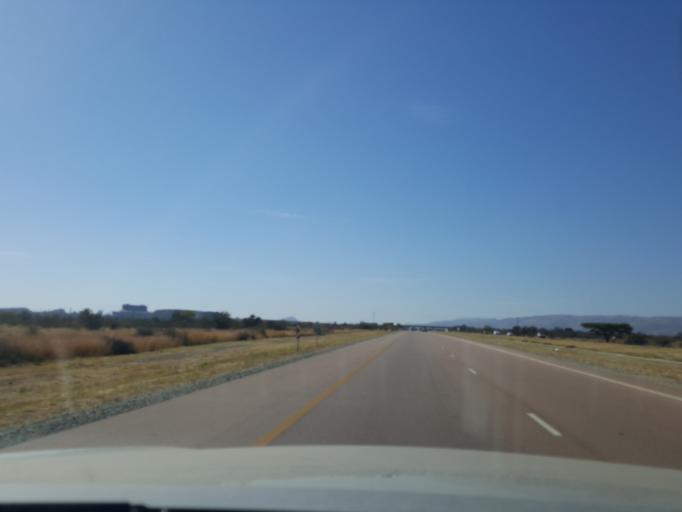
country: ZA
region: North-West
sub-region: Bojanala Platinum District Municipality
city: Brits
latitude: -25.7371
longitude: 27.5872
